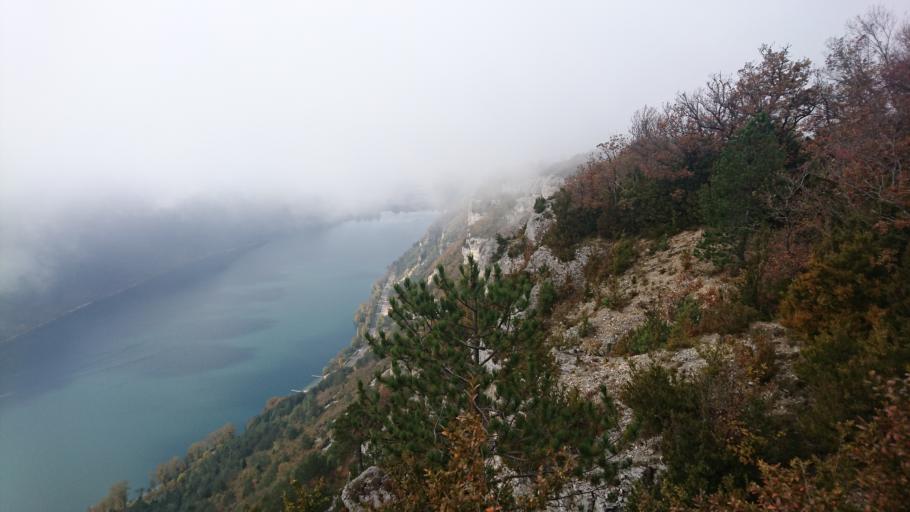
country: FR
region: Rhone-Alpes
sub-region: Departement de l'Ain
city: Nantua
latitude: 46.1621
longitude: 5.6085
